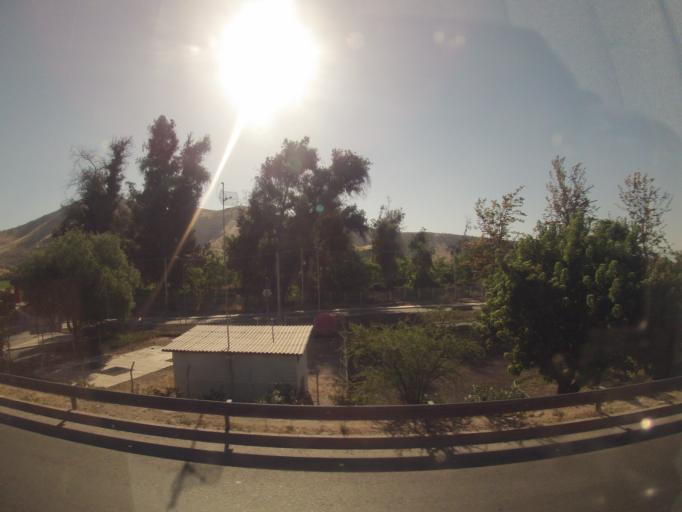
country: CL
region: Santiago Metropolitan
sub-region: Provincia de Maipo
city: San Bernardo
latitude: -33.5874
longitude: -70.7146
